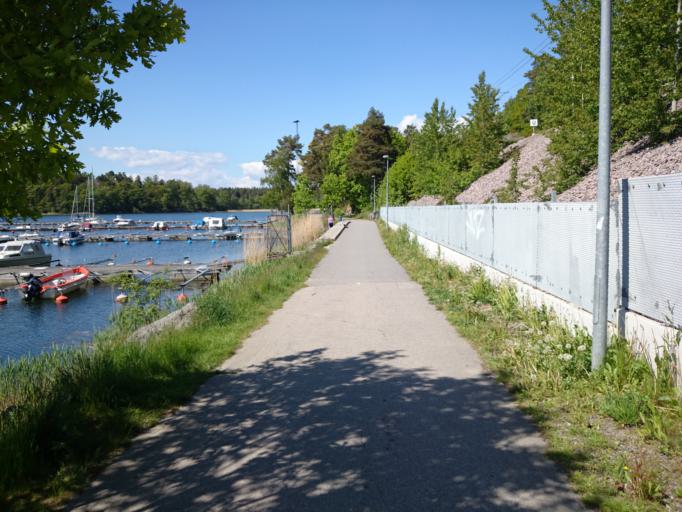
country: SE
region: Stockholm
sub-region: Nynashamns Kommun
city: Nynashamn
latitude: 58.8998
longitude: 17.9313
